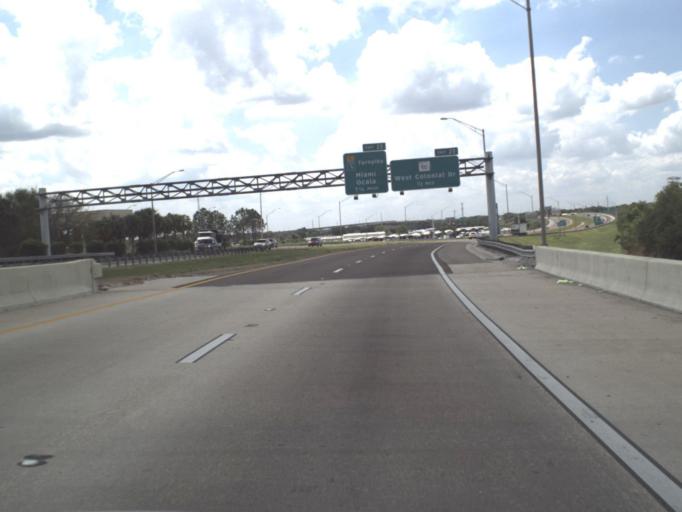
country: US
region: Florida
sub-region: Orange County
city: Ocoee
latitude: 28.5694
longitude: -81.5570
